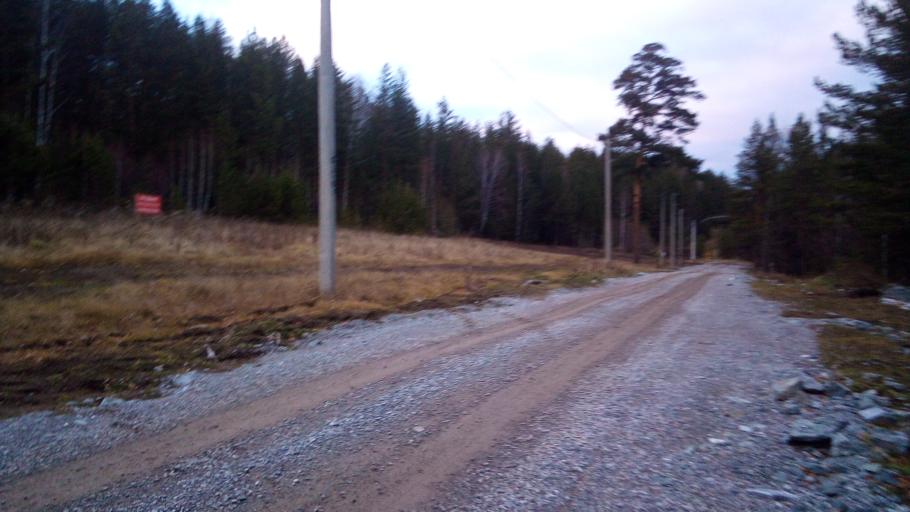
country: RU
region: Chelyabinsk
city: Turgoyak
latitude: 55.1782
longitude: 60.1313
